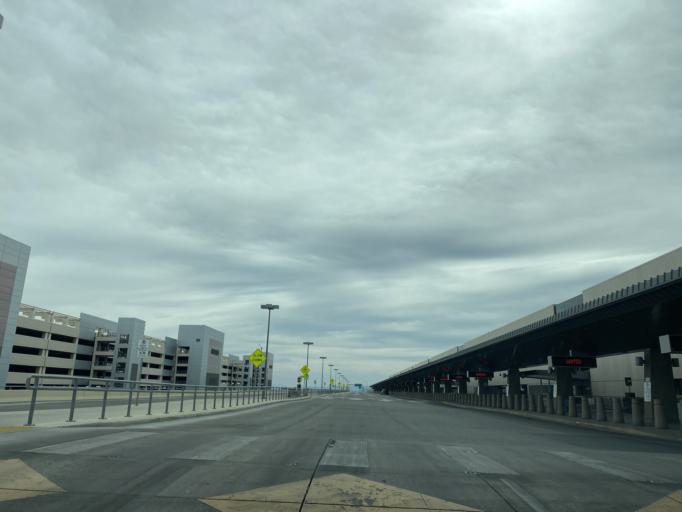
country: US
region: Nevada
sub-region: Clark County
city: Paradise
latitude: 36.0868
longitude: -115.1395
